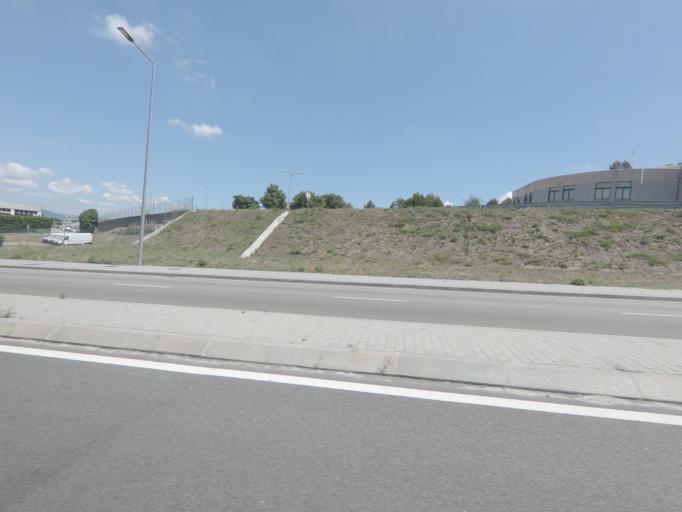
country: PT
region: Porto
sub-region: Paredes
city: Paredes
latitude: 41.1962
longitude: -8.3067
